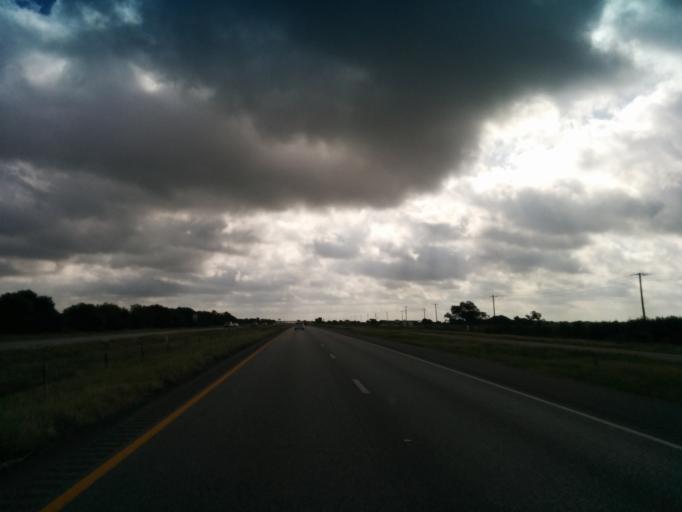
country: US
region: Texas
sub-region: Guadalupe County
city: Marion
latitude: 29.5138
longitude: -98.1525
